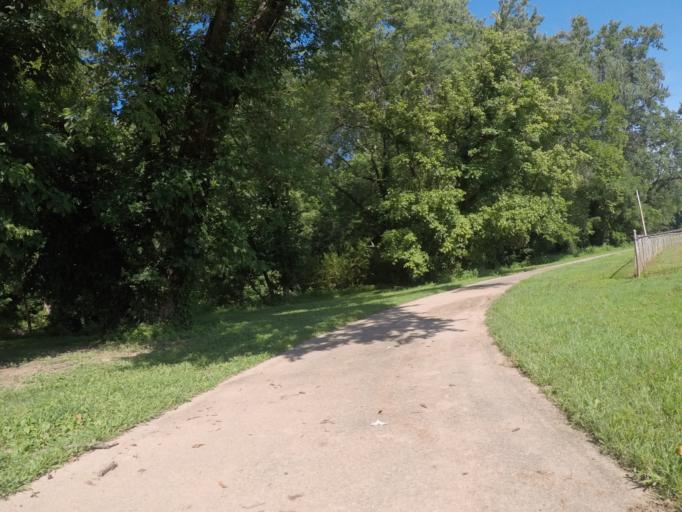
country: US
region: West Virginia
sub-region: Cabell County
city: Huntington
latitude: 38.4027
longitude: -82.4867
